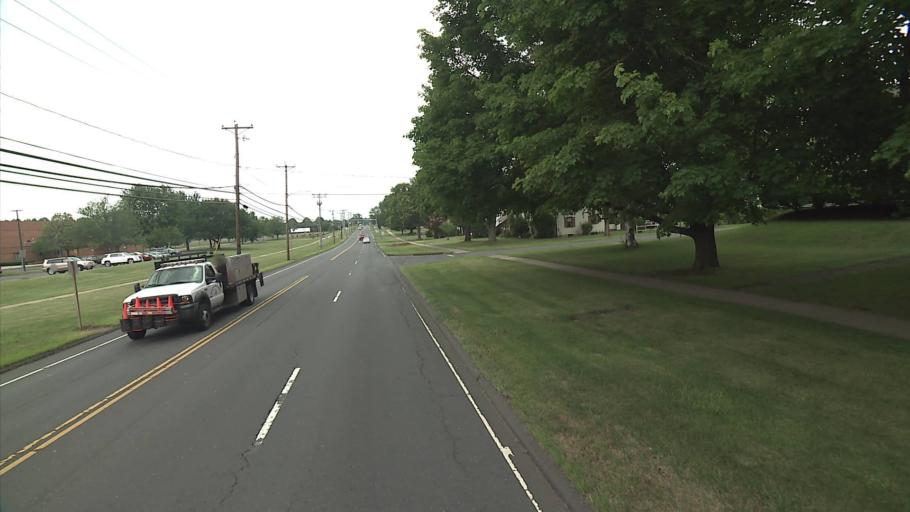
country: US
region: Connecticut
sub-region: Hartford County
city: Newington
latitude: 41.7004
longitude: -72.7344
